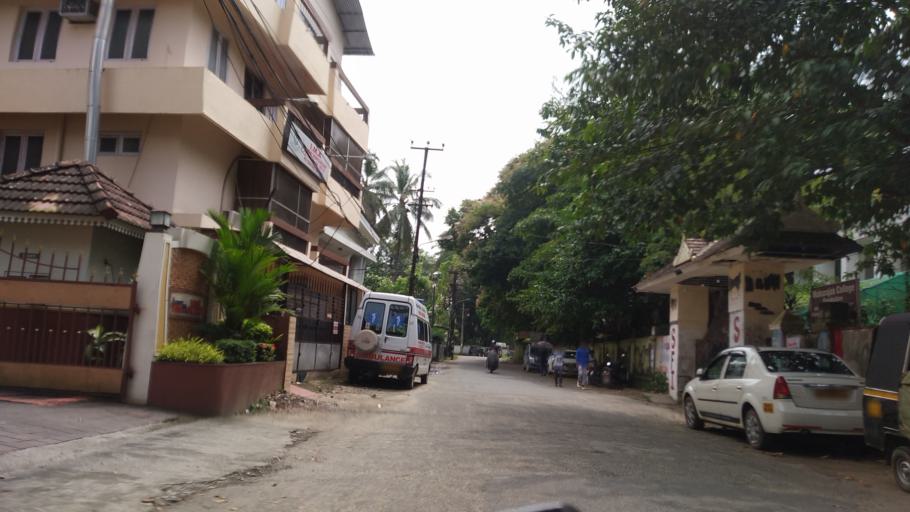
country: IN
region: Kerala
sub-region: Ernakulam
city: Cochin
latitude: 9.9708
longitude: 76.2830
